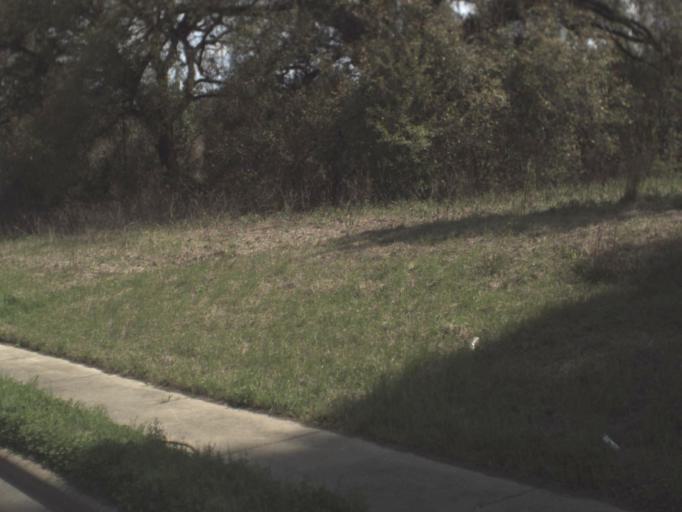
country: US
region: Florida
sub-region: Gadsden County
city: Havana
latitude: 30.6515
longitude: -84.4168
